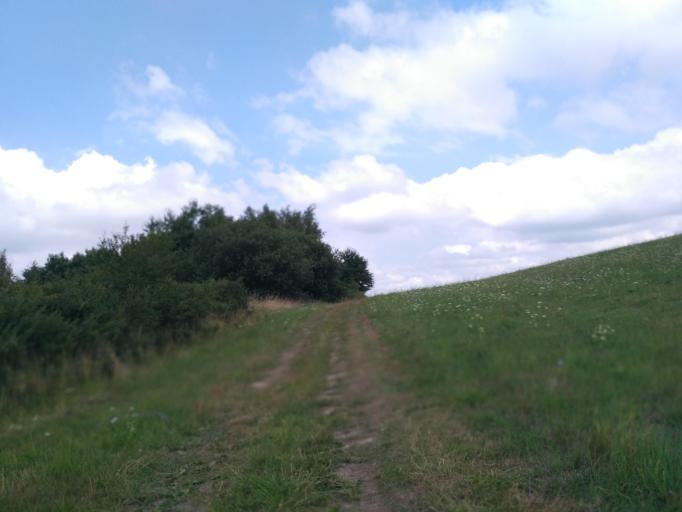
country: PL
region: Subcarpathian Voivodeship
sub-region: Powiat krosnienski
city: Iwonicz-Zdroj
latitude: 49.5820
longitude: 21.8066
